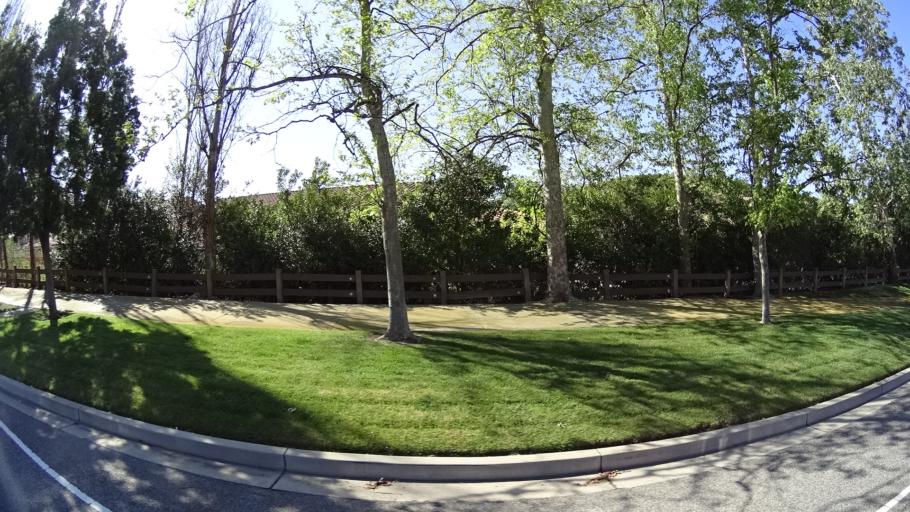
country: US
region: California
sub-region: Ventura County
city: Simi Valley
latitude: 34.2512
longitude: -118.8230
